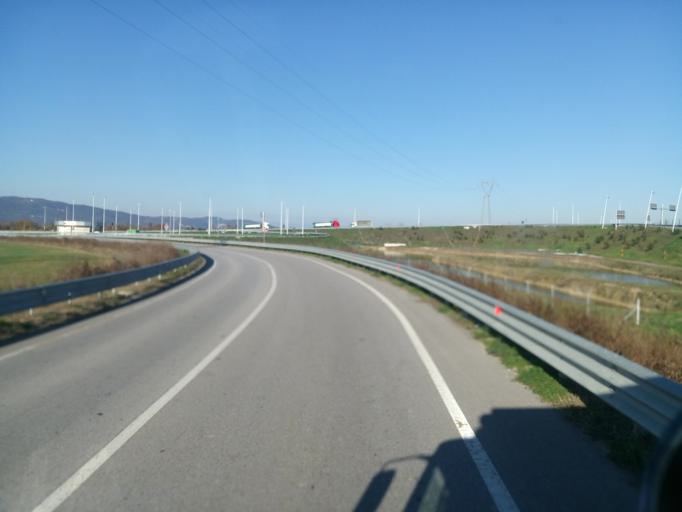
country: IT
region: Veneto
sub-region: Provincia di Vicenza
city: Ponte di Barbarano
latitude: 45.3845
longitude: 11.6116
